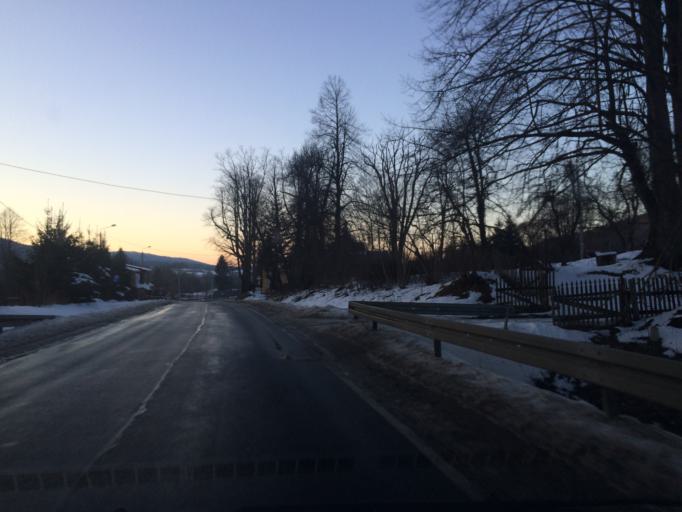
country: PL
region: Subcarpathian Voivodeship
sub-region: Powiat bieszczadzki
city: Czarna
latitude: 49.3652
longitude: 22.6623
